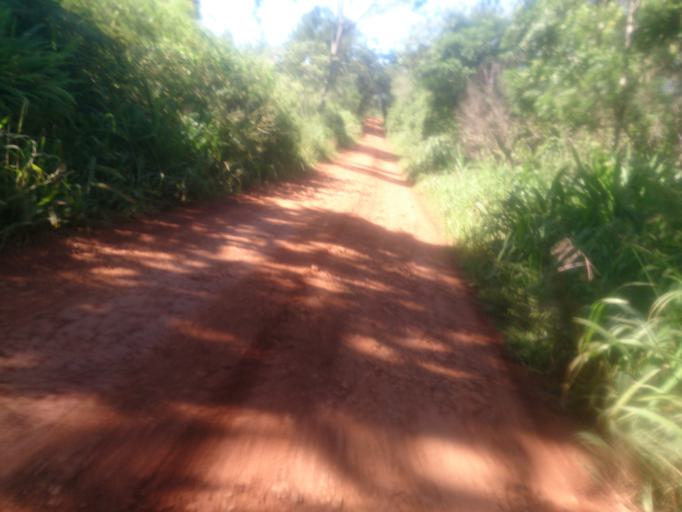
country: AR
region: Misiones
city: General Alvear
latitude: -27.4352
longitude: -55.1147
